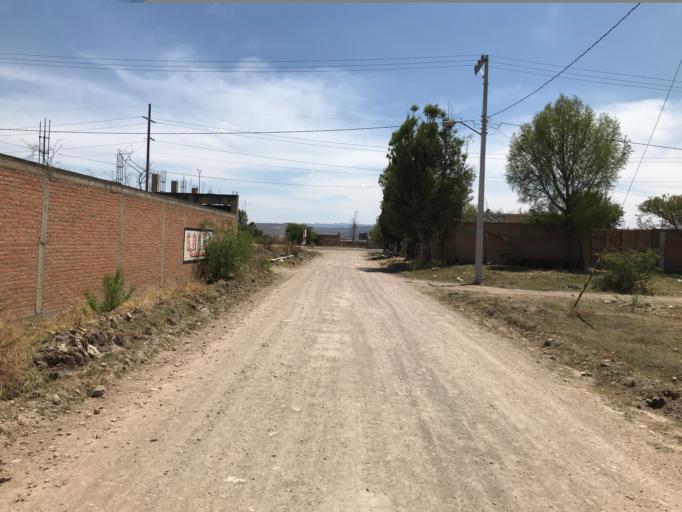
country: MX
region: Durango
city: Victoria de Durango
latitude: 23.9788
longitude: -104.6834
